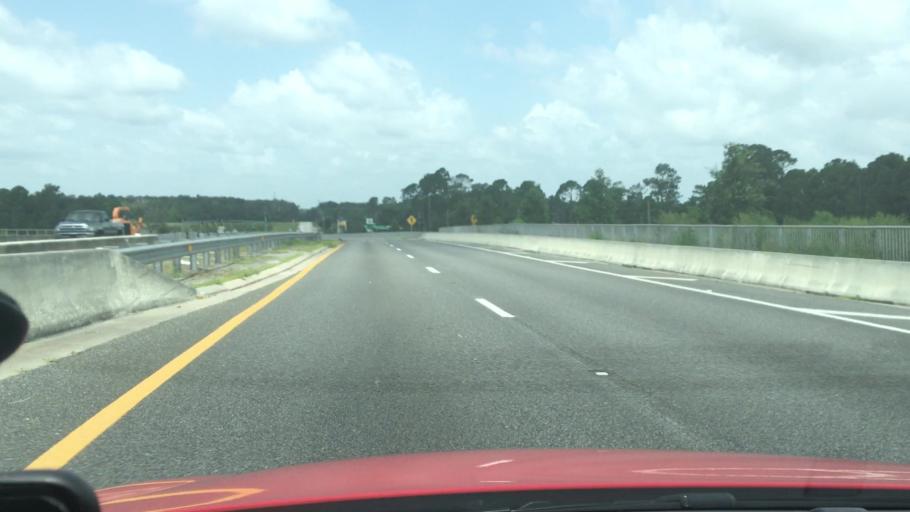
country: US
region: Florida
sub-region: Volusia County
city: Lake Helen
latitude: 29.0176
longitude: -81.2325
